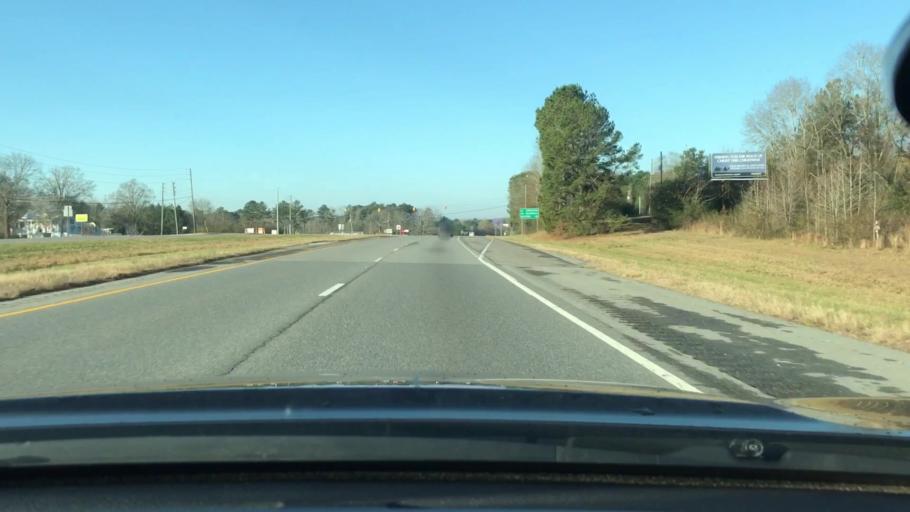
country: US
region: Alabama
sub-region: Shelby County
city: Westover
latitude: 33.3512
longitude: -86.5338
